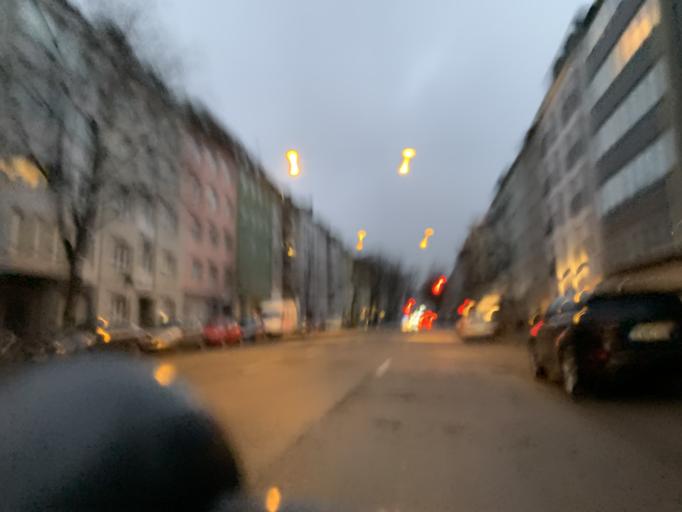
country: DE
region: North Rhine-Westphalia
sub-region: Regierungsbezirk Dusseldorf
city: Dusseldorf
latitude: 51.2376
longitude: 6.7901
